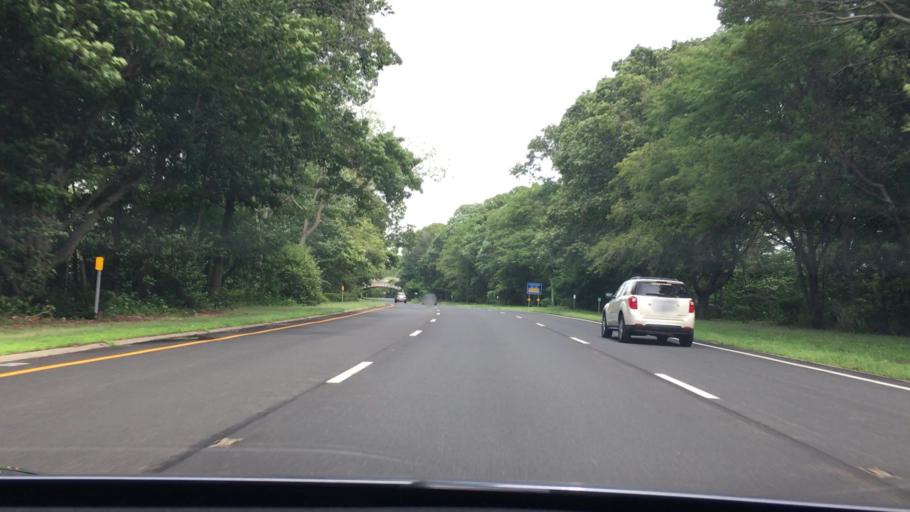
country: US
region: New York
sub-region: Nassau County
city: Wantagh
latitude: 40.6902
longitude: -73.5159
